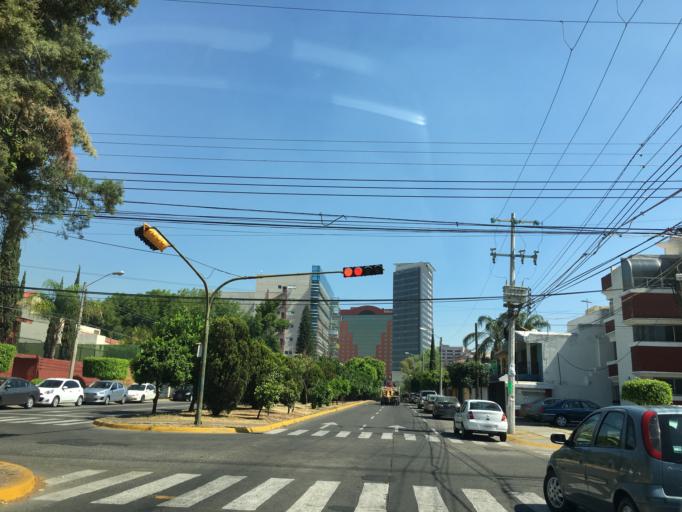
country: MX
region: Jalisco
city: Guadalajara
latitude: 20.6496
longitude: -103.3895
